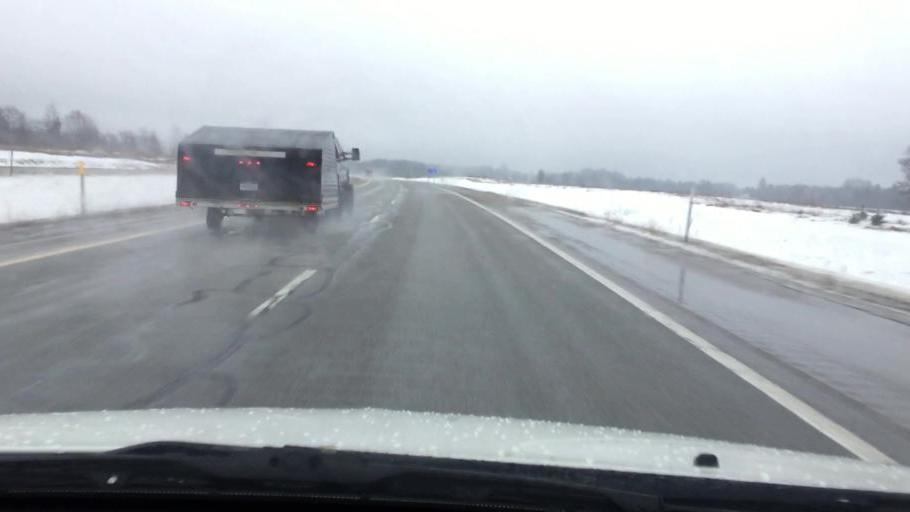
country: US
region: Michigan
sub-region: Wexford County
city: Cadillac
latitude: 44.2619
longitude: -85.3851
